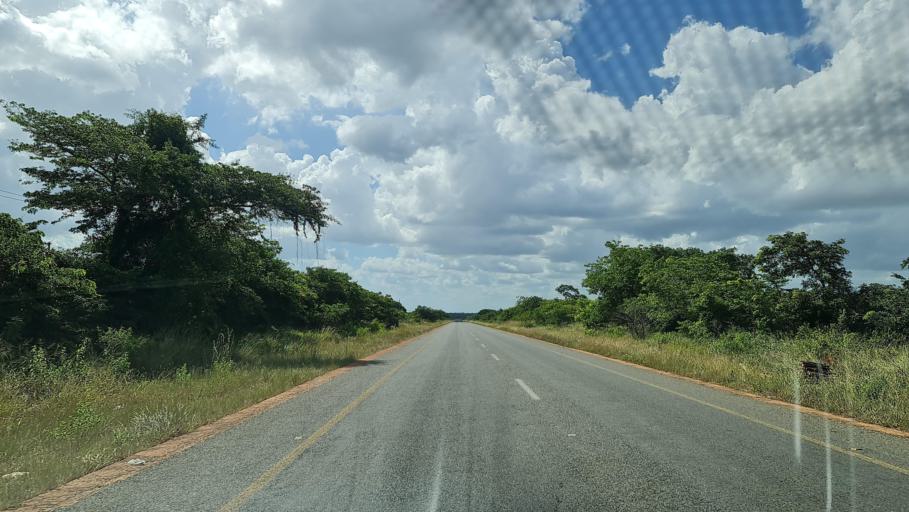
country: MZ
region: Inhambane
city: Maxixe
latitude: -22.9704
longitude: 35.2171
